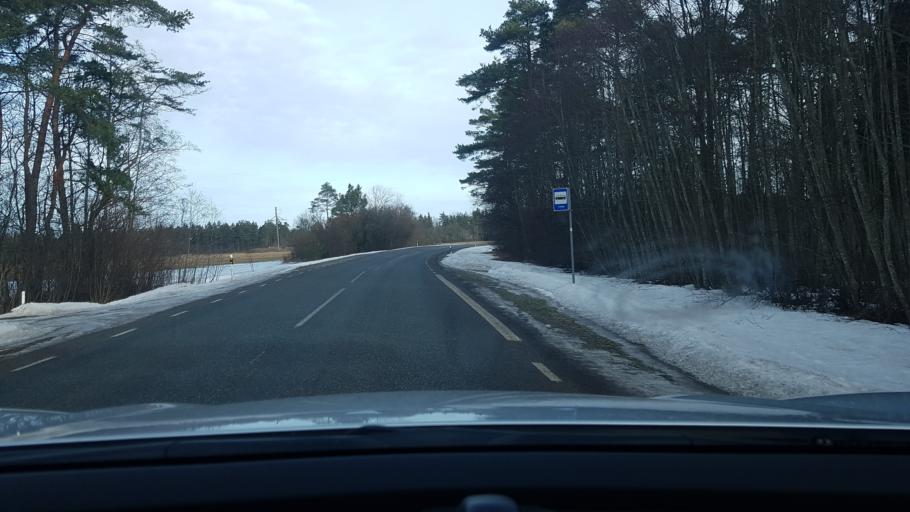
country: EE
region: Saare
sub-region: Kuressaare linn
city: Kuressaare
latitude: 58.4021
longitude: 22.6430
